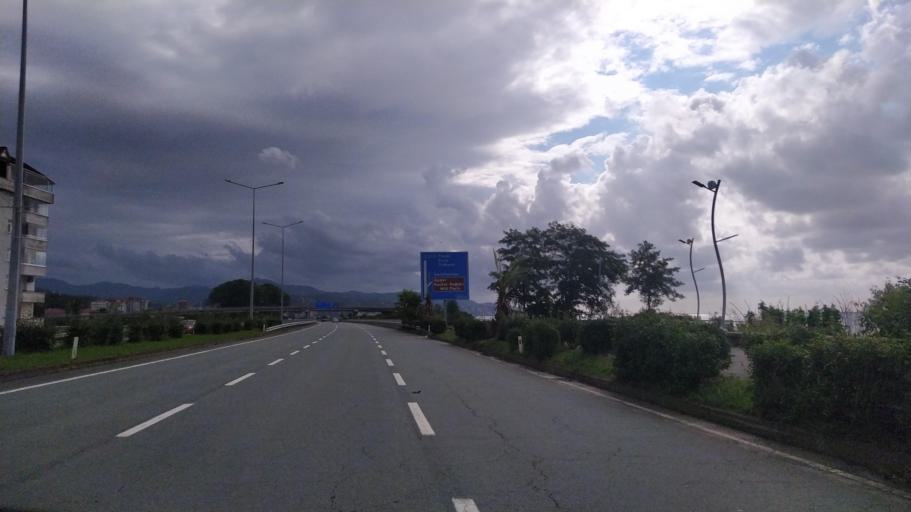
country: TR
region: Rize
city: Ardesen
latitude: 41.1897
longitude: 40.9642
